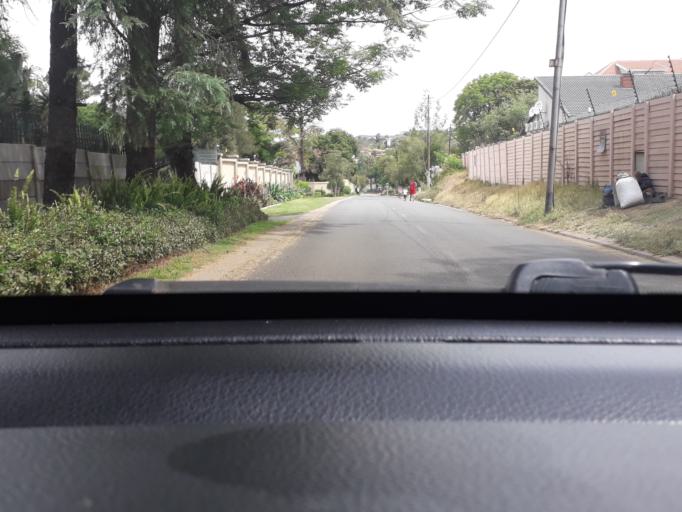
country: ZA
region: Gauteng
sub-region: City of Johannesburg Metropolitan Municipality
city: Midrand
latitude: -26.0632
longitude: 28.0636
